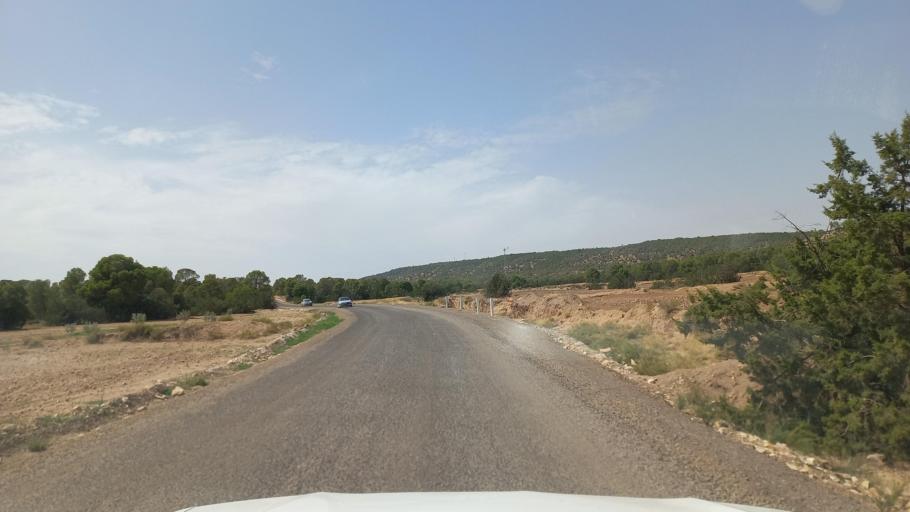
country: TN
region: Al Qasrayn
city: Sbiba
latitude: 35.3838
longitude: 8.9359
